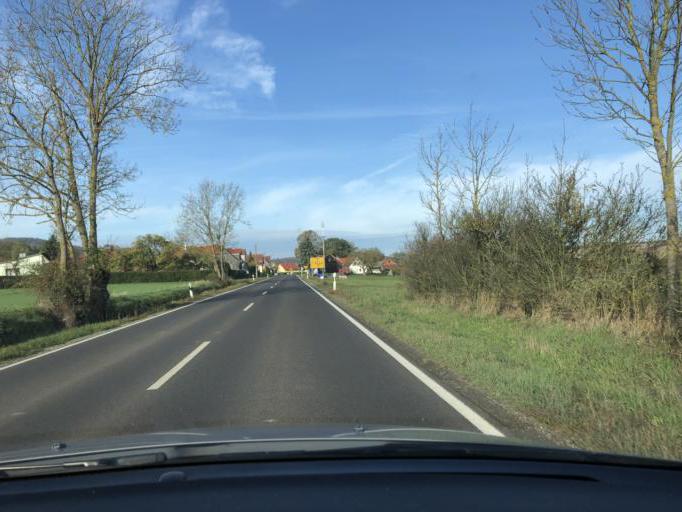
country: DE
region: Thuringia
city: Reurieth
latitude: 50.4114
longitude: 10.6378
